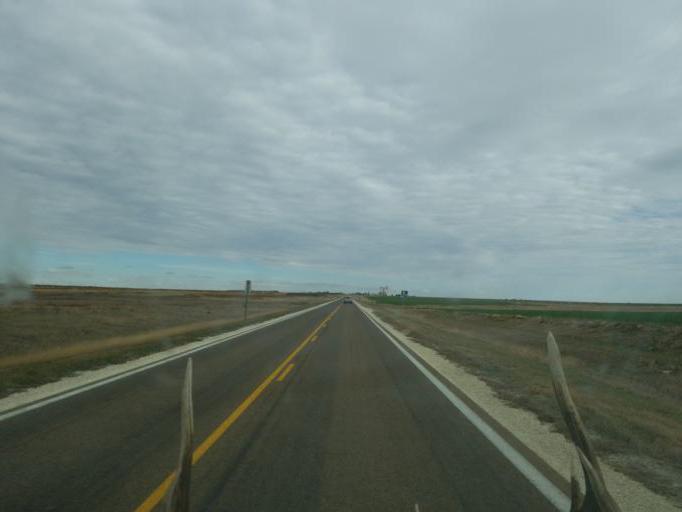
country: US
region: Kansas
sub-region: Logan County
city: Oakley
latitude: 39.0815
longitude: -101.1807
